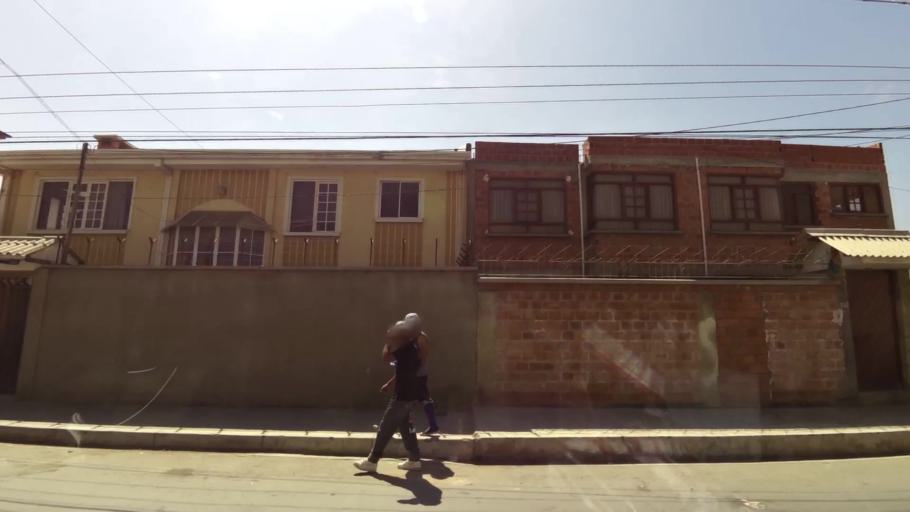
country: BO
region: La Paz
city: La Paz
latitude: -16.5402
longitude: -68.0523
